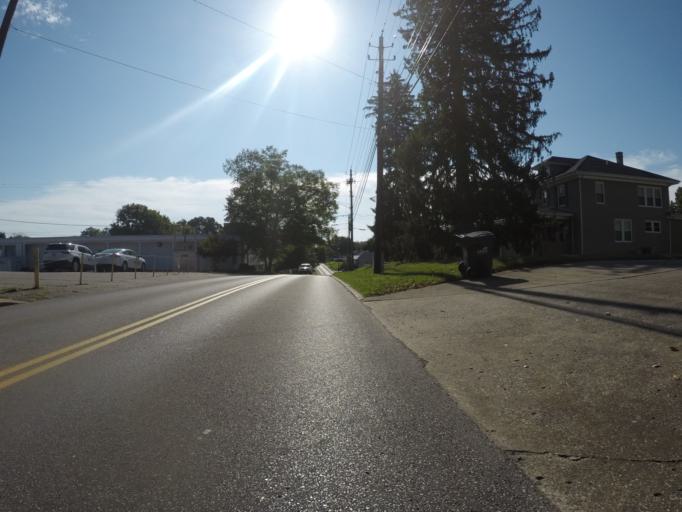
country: US
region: Kentucky
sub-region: Boyd County
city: Ashland
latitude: 38.4517
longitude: -82.6334
